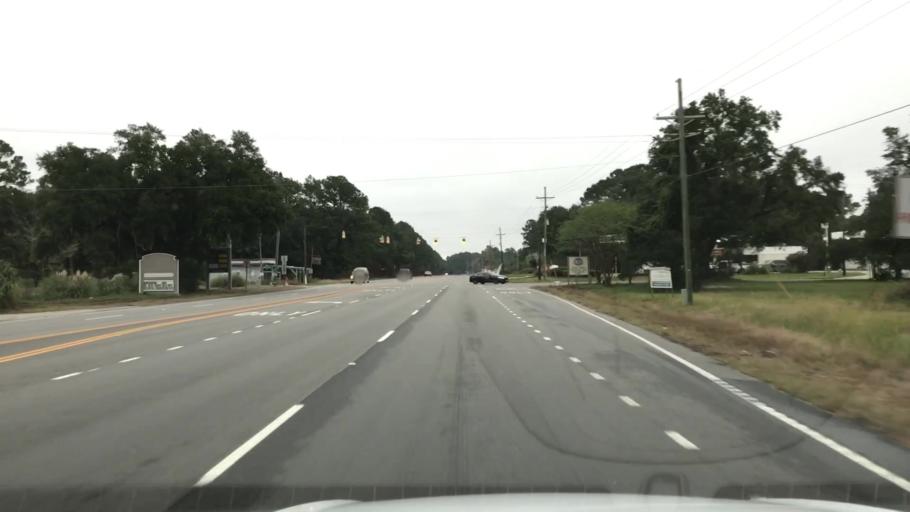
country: US
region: South Carolina
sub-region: Charleston County
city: Awendaw
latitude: 33.0947
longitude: -79.4770
